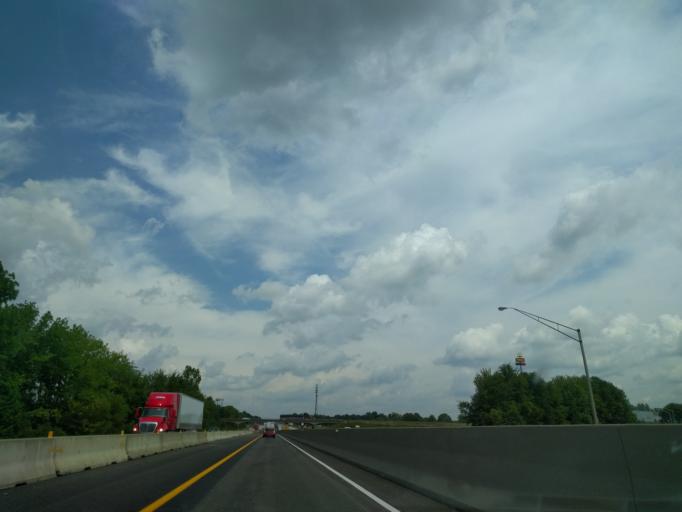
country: US
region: Kentucky
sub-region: Hardin County
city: Elizabethtown
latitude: 37.5932
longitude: -85.8694
